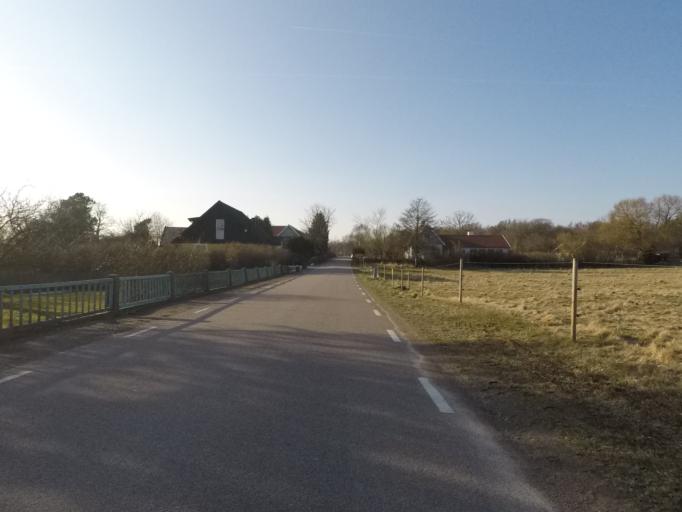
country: SE
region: Skane
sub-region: Hoganas Kommun
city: Hoganas
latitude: 56.2527
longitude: 12.6109
